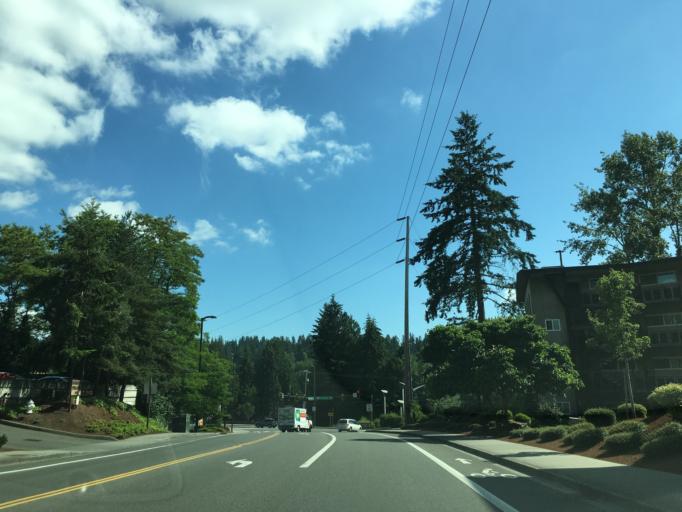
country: US
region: Washington
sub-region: King County
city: Kenmore
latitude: 47.7567
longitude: -122.2337
